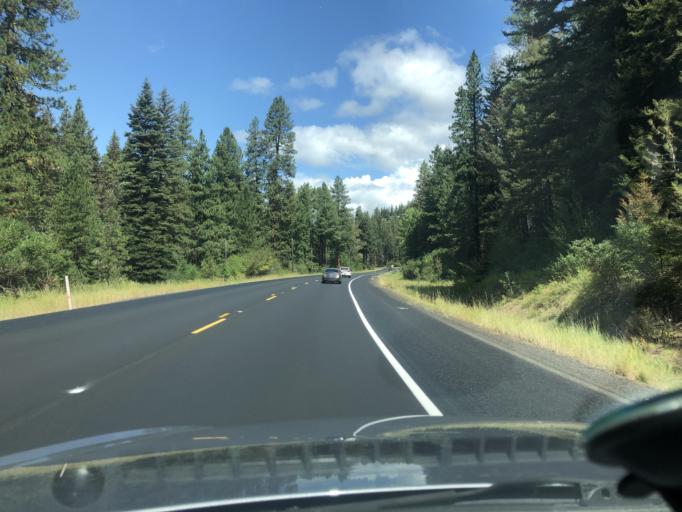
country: US
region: Washington
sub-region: Kittitas County
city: Cle Elum
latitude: 47.2830
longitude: -120.6979
